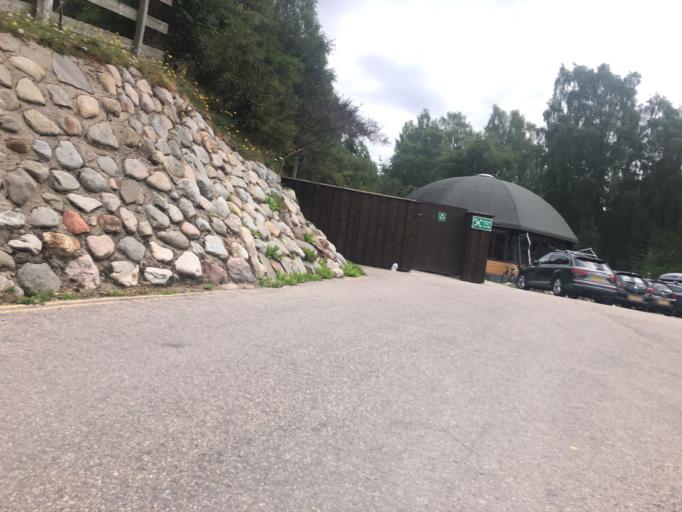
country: GB
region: Scotland
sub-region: Highland
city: Aviemore
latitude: 57.1168
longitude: -3.9204
